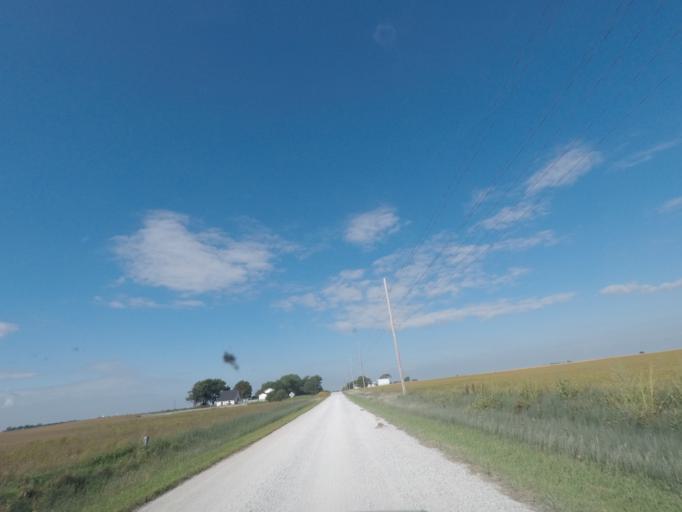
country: US
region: Iowa
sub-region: Story County
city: Nevada
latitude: 42.0345
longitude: -93.4073
